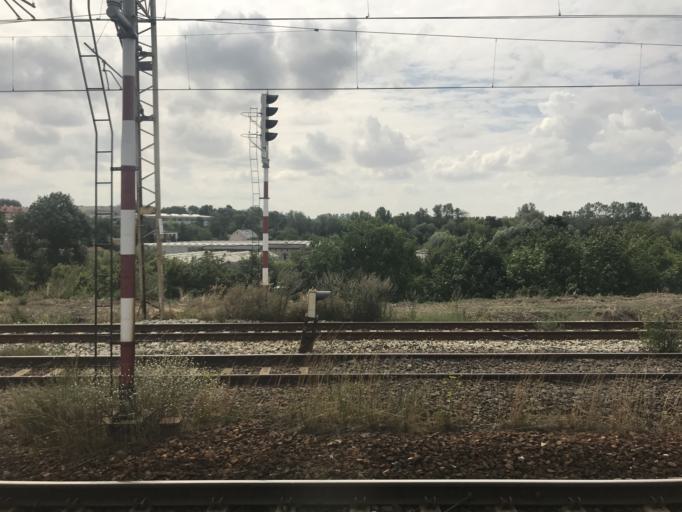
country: PL
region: Greater Poland Voivodeship
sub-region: Powiat gnieznienski
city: Gniezno
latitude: 52.5286
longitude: 17.5921
